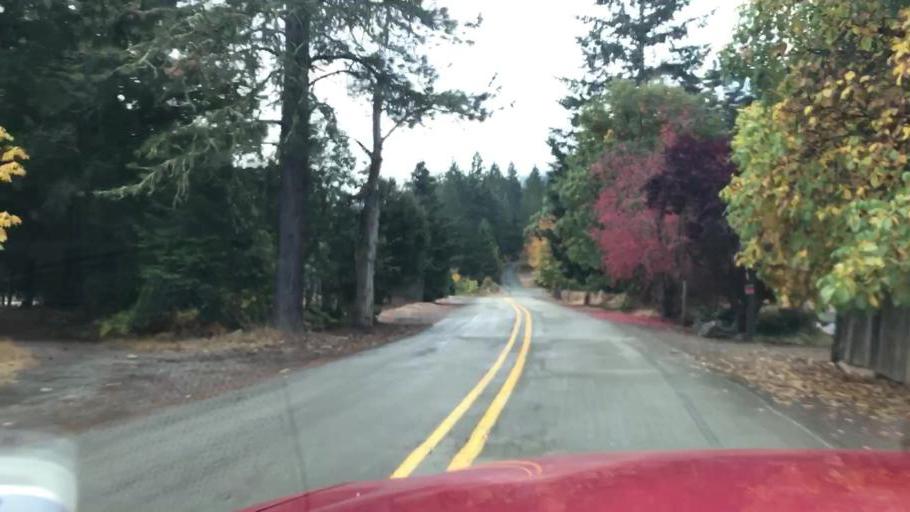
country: US
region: Oregon
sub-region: Douglas County
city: Canyonville
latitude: 42.7645
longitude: -123.3325
